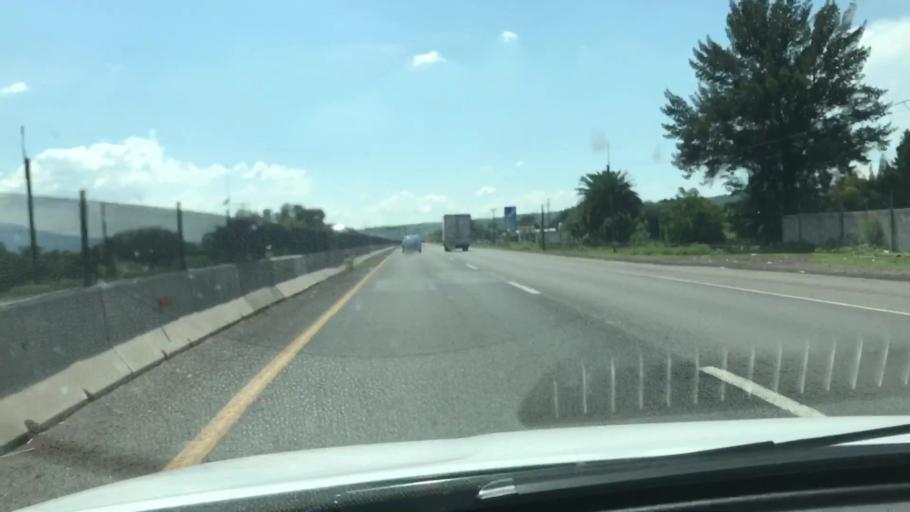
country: MX
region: Guanajuato
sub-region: Penjamo
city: Estacion la Piedad
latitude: 20.3889
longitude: -101.9407
